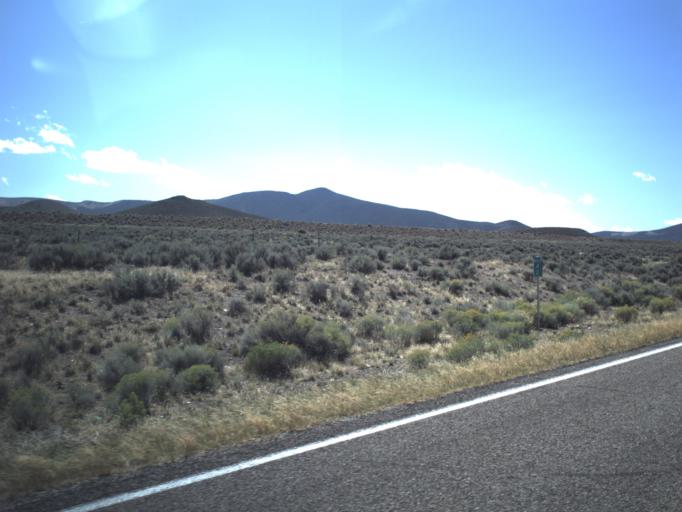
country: US
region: Utah
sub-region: Beaver County
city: Milford
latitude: 38.2056
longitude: -112.9269
